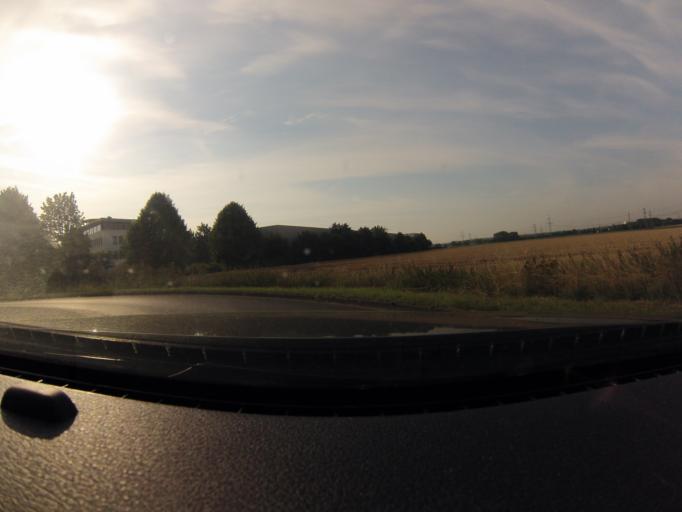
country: DE
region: North Rhine-Westphalia
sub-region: Regierungsbezirk Koln
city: Frechen
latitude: 50.9139
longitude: 6.8522
